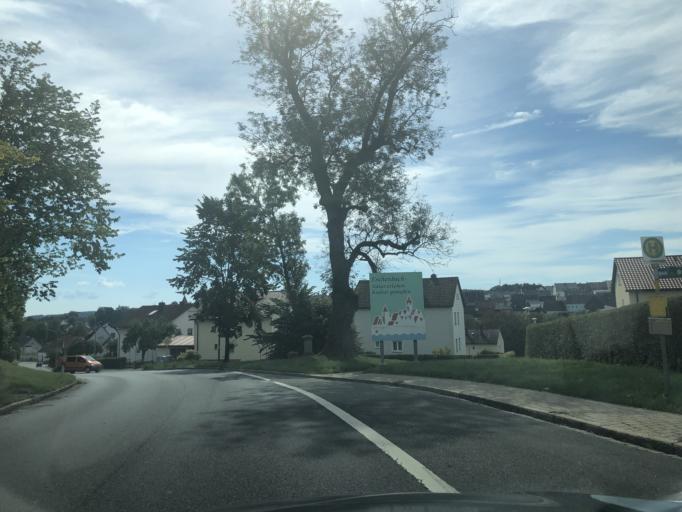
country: DE
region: Bavaria
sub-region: Upper Palatinate
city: Speinshart
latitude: 49.7569
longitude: 11.8288
